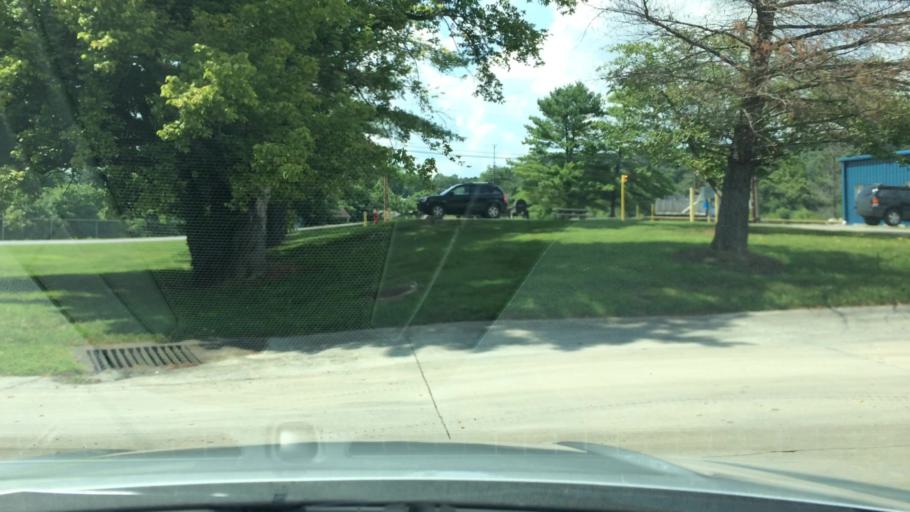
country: US
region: Kentucky
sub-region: Pulaski County
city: Somerset
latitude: 36.9707
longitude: -84.5868
